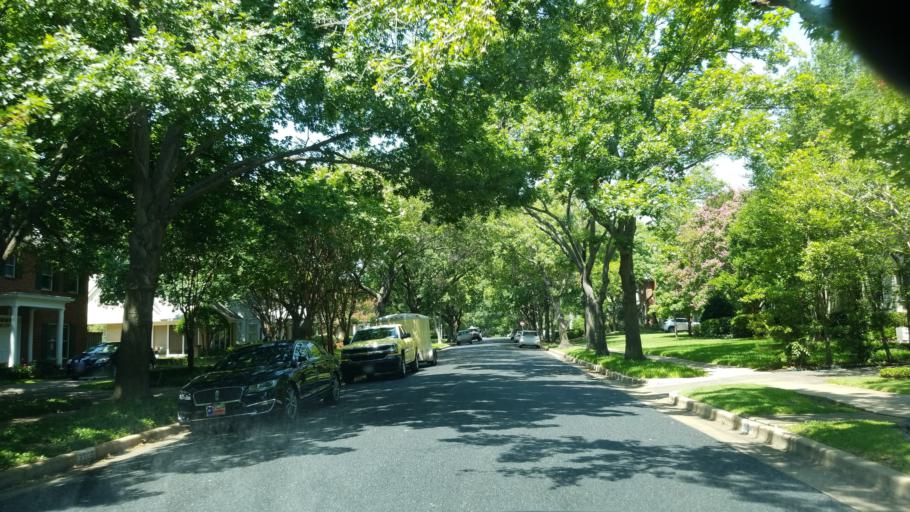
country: US
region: Texas
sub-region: Dallas County
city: Highland Park
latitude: 32.8335
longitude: -96.7855
